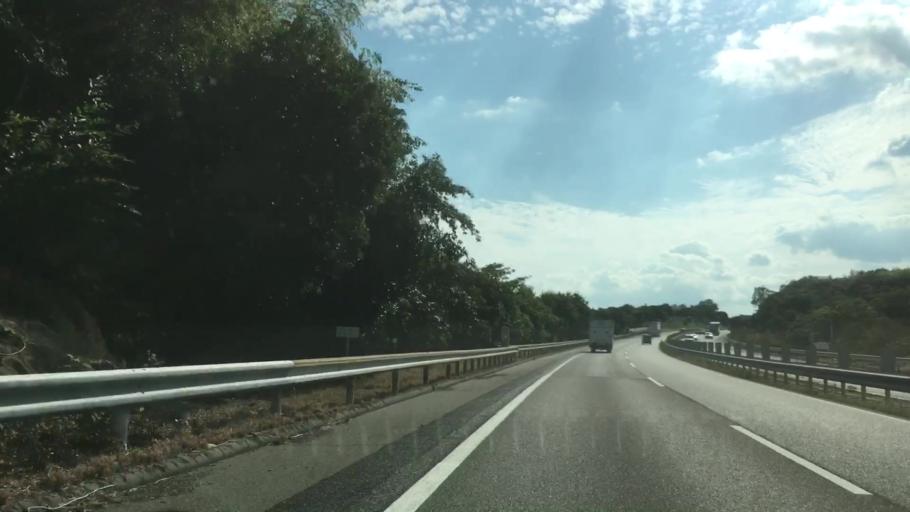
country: JP
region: Hiroshima
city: Ono-hara
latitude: 34.2790
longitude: 132.2576
